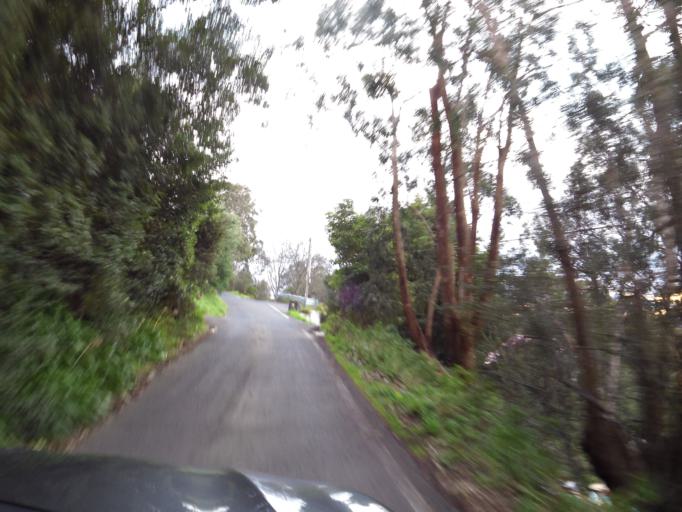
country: AU
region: Victoria
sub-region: Knox
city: Ferntree Gully
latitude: -37.8961
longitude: 145.3054
